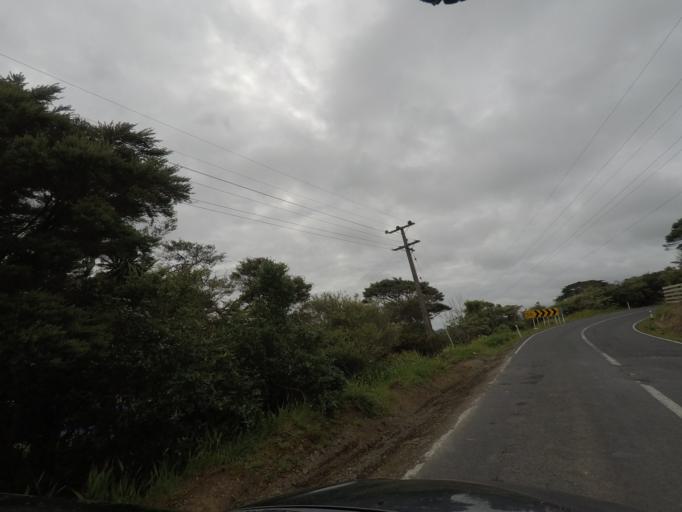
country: NZ
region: Auckland
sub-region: Auckland
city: Rosebank
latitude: -36.8113
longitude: 174.5778
